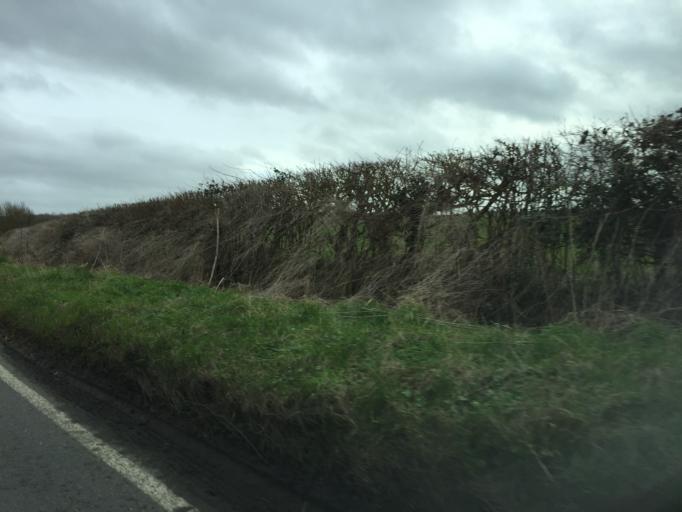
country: GB
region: England
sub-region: Gloucestershire
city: Lechlade
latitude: 51.6771
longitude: -1.6712
